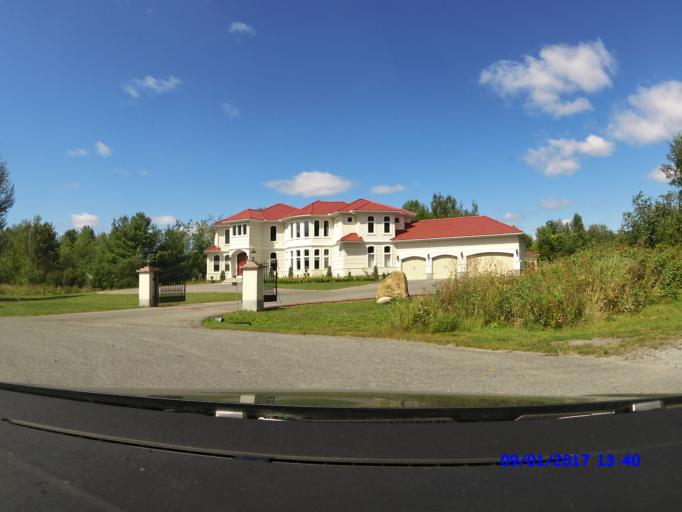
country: CA
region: Ontario
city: Bells Corners
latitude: 45.3600
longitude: -75.9727
